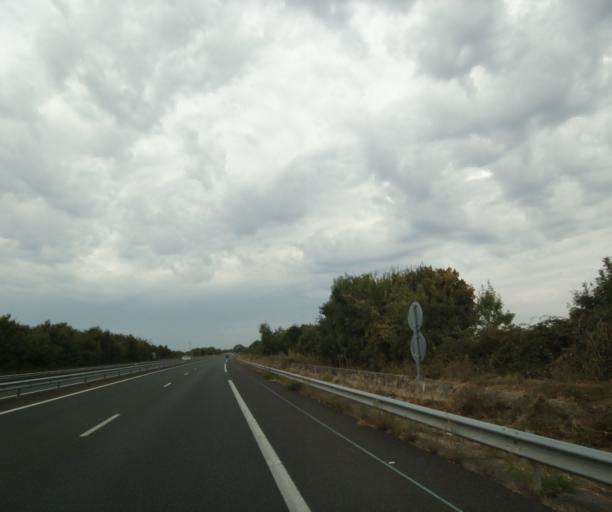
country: FR
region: Poitou-Charentes
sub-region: Departement de la Charente-Maritime
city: Tonnay-Charente
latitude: 45.9549
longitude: -0.9029
